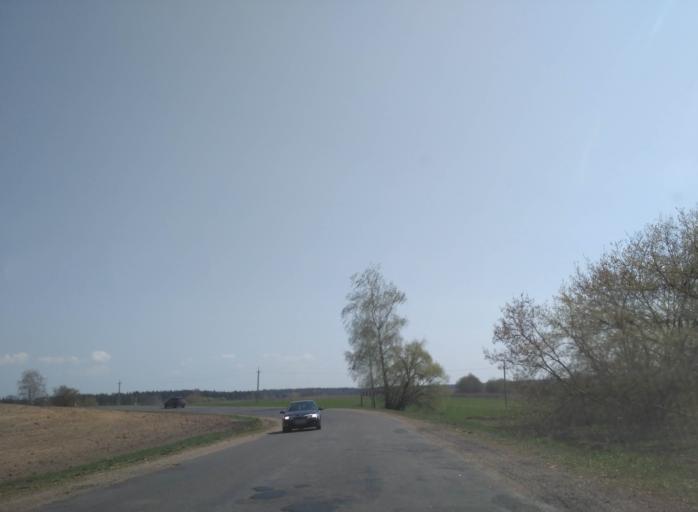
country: BY
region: Minsk
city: Horad Barysaw
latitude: 54.3146
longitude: 28.5540
